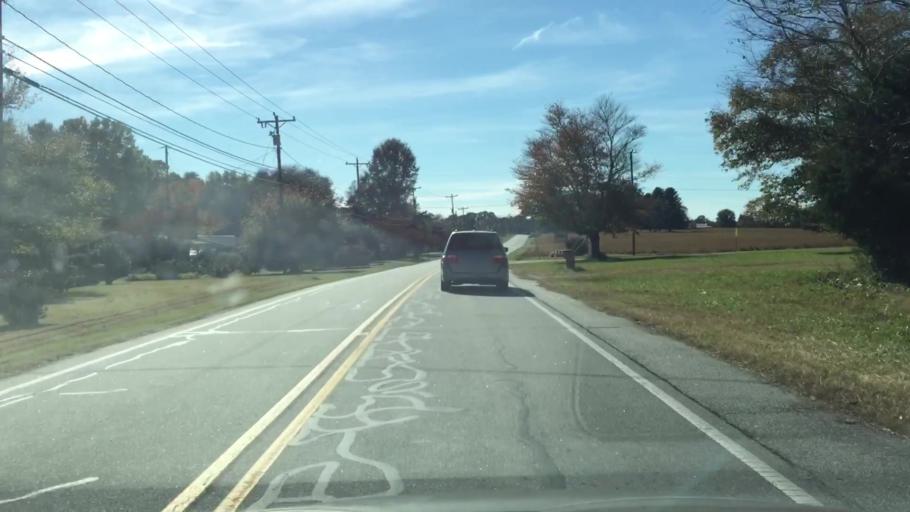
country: US
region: North Carolina
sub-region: Rowan County
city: China Grove
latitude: 35.6560
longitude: -80.5662
